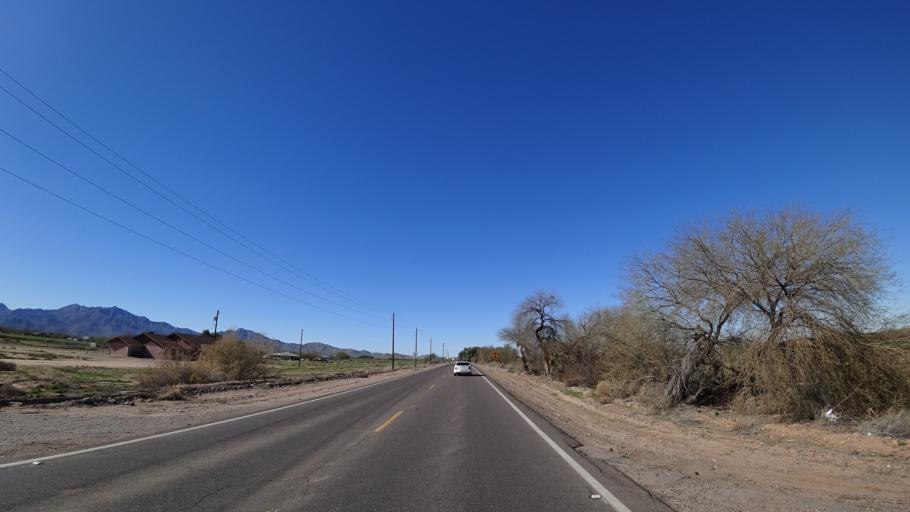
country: US
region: Arizona
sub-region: Maricopa County
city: Tolleson
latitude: 33.3773
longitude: -112.2518
